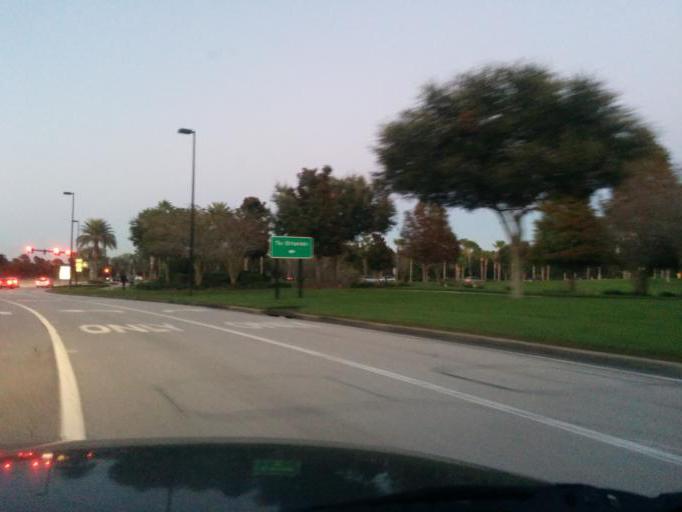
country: US
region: Florida
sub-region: Orange County
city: Williamsburg
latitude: 28.4321
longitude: -81.4636
